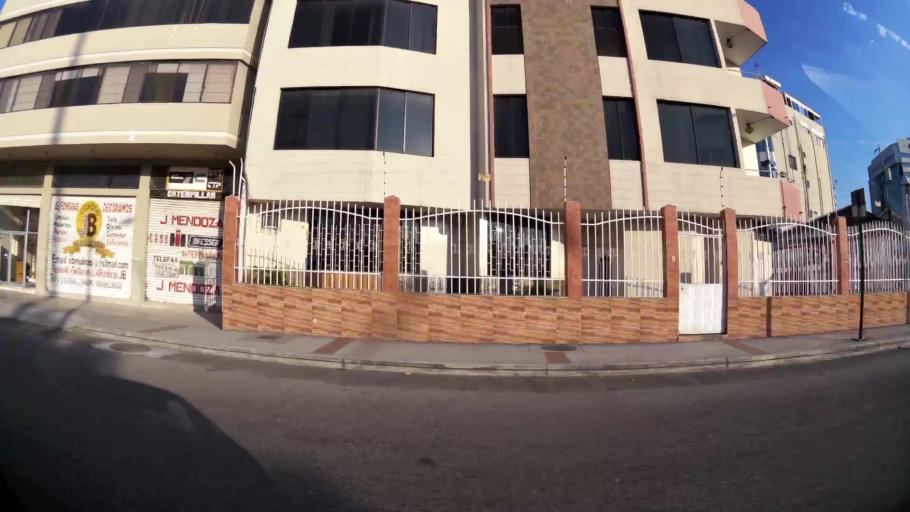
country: EC
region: Guayas
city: Eloy Alfaro
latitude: -2.1564
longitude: -79.8956
